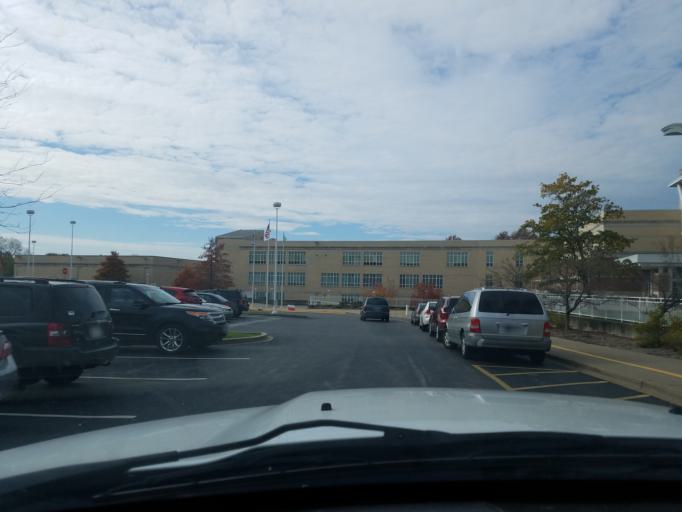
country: US
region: Indiana
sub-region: Floyd County
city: New Albany
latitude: 38.2986
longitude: -85.8102
